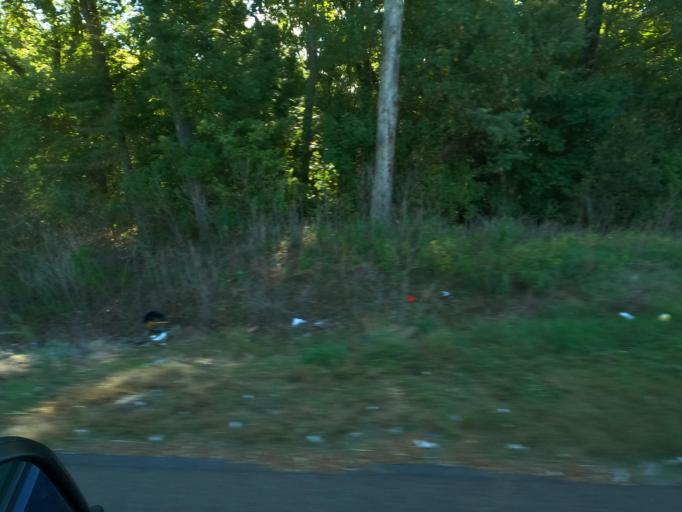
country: US
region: Tennessee
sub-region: Tipton County
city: Atoka
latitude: 35.4544
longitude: -89.7754
